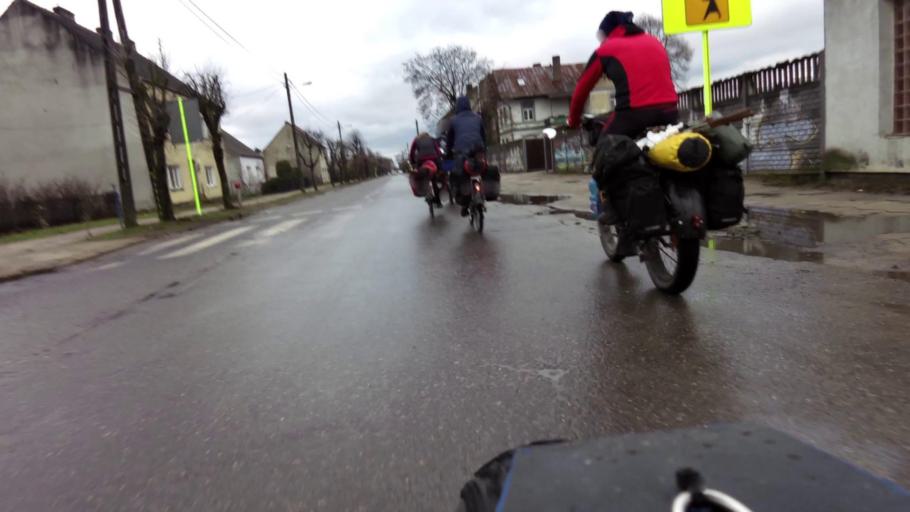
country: PL
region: Lubusz
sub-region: Powiat gorzowski
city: Witnica
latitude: 52.6787
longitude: 14.8921
